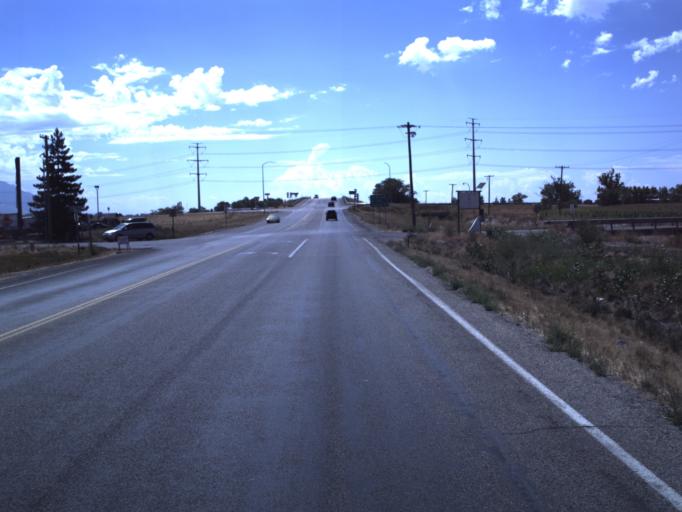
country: US
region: Utah
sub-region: Box Elder County
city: Elwood
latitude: 41.6840
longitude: -112.1414
